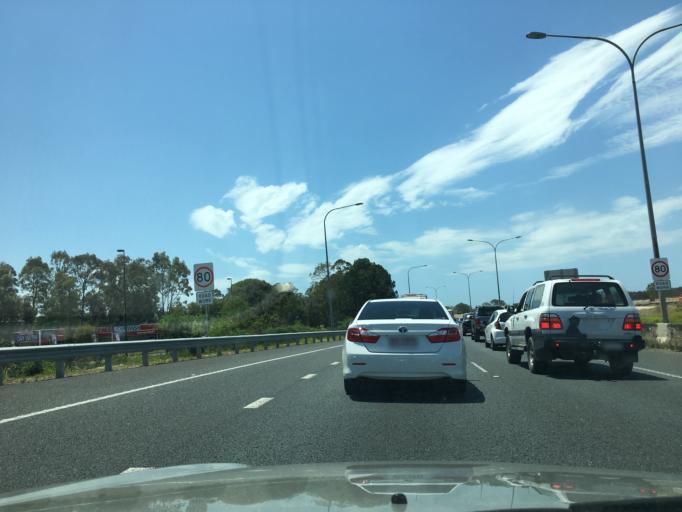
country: AU
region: Queensland
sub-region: Brisbane
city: Wavell Heights
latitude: -27.3779
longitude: 153.0947
